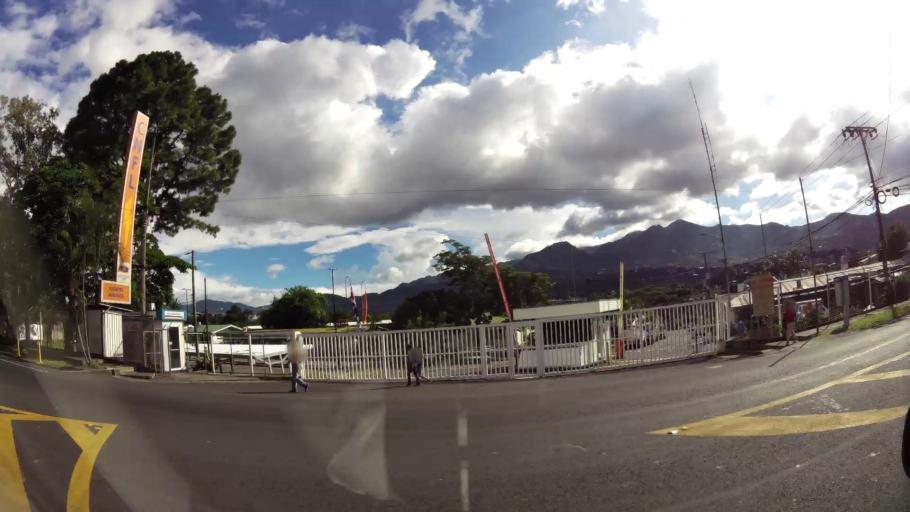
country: CR
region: San Jose
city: San Rafael
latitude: 9.9334
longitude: -84.1178
